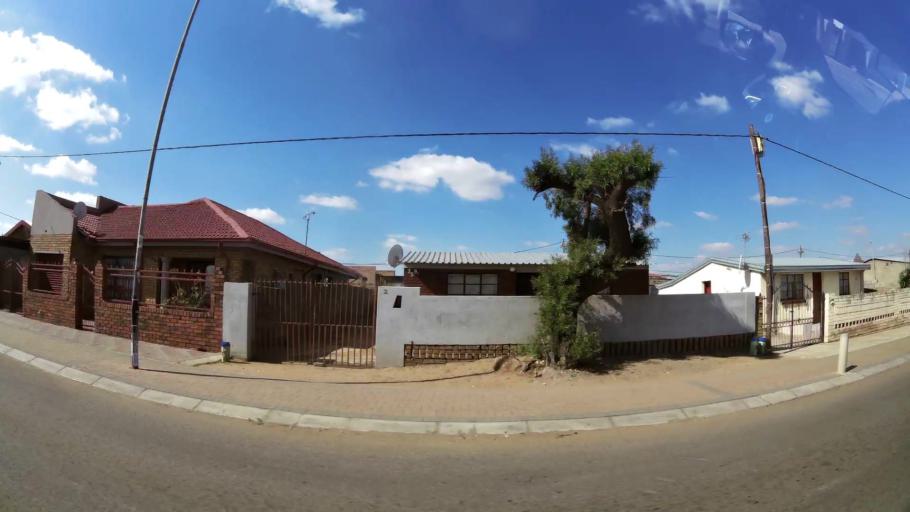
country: ZA
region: Gauteng
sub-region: West Rand District Municipality
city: Krugersdorp
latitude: -26.1565
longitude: 27.7843
